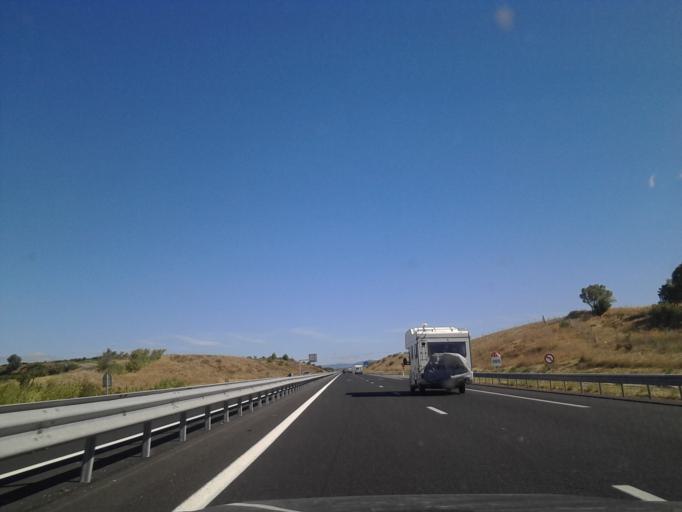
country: FR
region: Languedoc-Roussillon
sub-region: Departement de l'Herault
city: Paulhan
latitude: 43.5252
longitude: 3.4435
